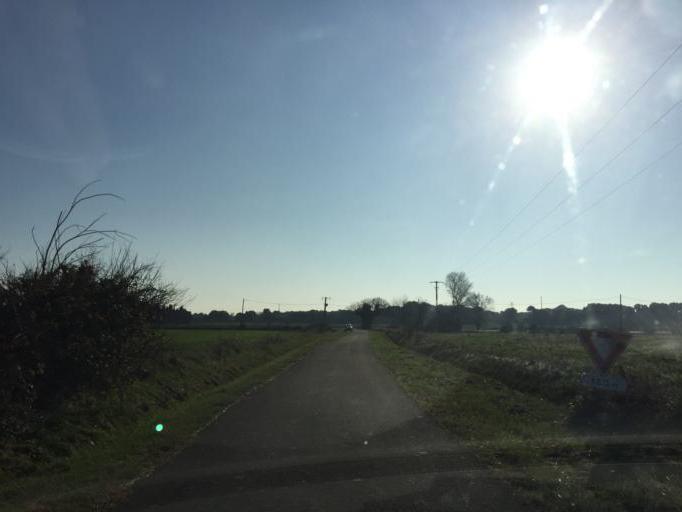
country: FR
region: Provence-Alpes-Cote d'Azur
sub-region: Departement du Vaucluse
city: Courthezon
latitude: 44.1192
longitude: 4.8581
